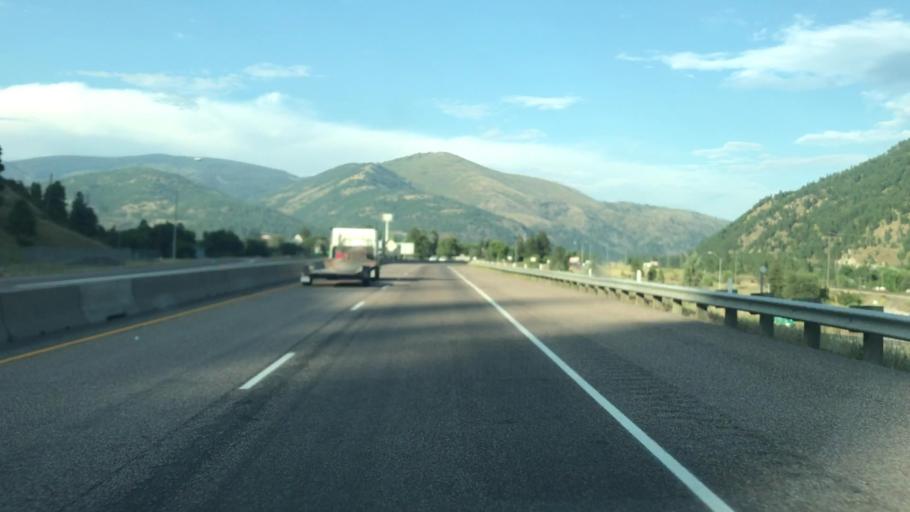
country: US
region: Montana
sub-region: Missoula County
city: East Missoula
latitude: 46.8657
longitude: -113.9536
